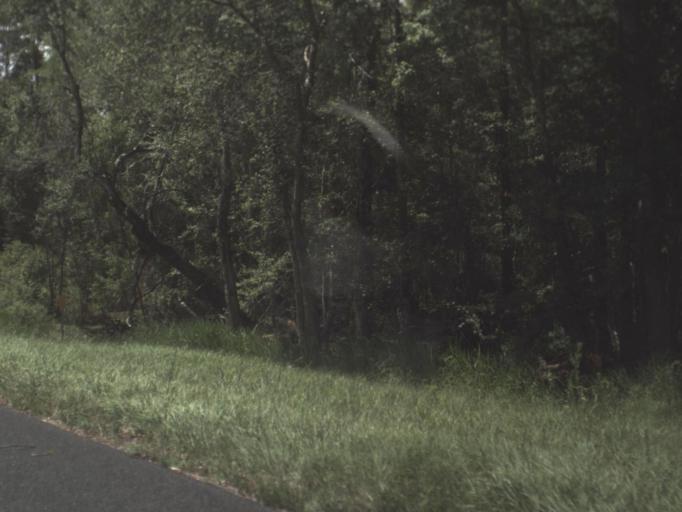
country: US
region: Florida
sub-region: Taylor County
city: Perry
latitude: 30.1849
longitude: -83.6416
